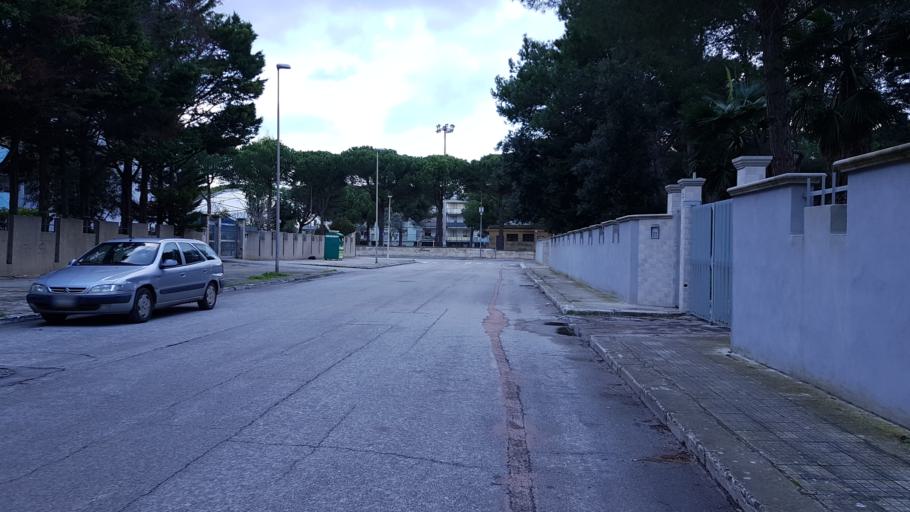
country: IT
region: Apulia
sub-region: Provincia di Brindisi
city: Brindisi
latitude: 40.6186
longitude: 17.9190
